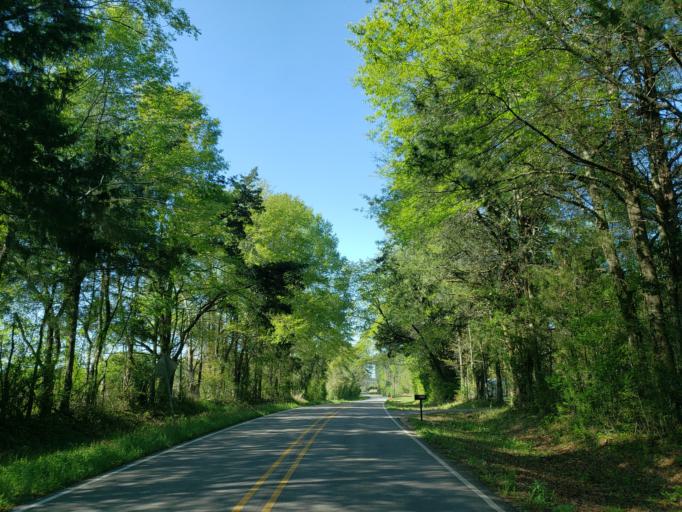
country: US
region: Mississippi
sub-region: Forrest County
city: Rawls Springs
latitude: 31.5423
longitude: -89.3653
